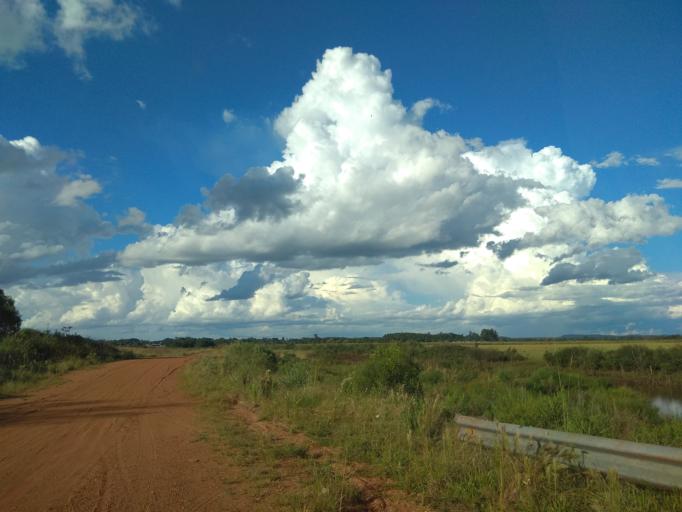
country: AR
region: Misiones
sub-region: Departamento de Candelaria
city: Candelaria
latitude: -27.4890
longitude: -55.7533
